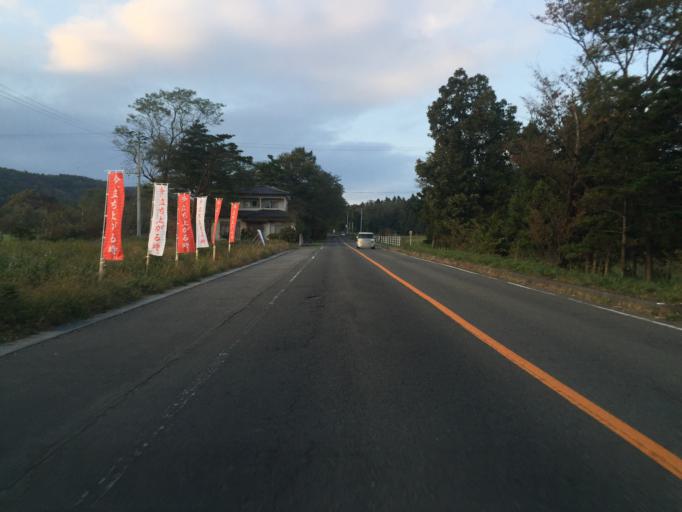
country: JP
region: Fukushima
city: Nihommatsu
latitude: 37.5951
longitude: 140.3566
